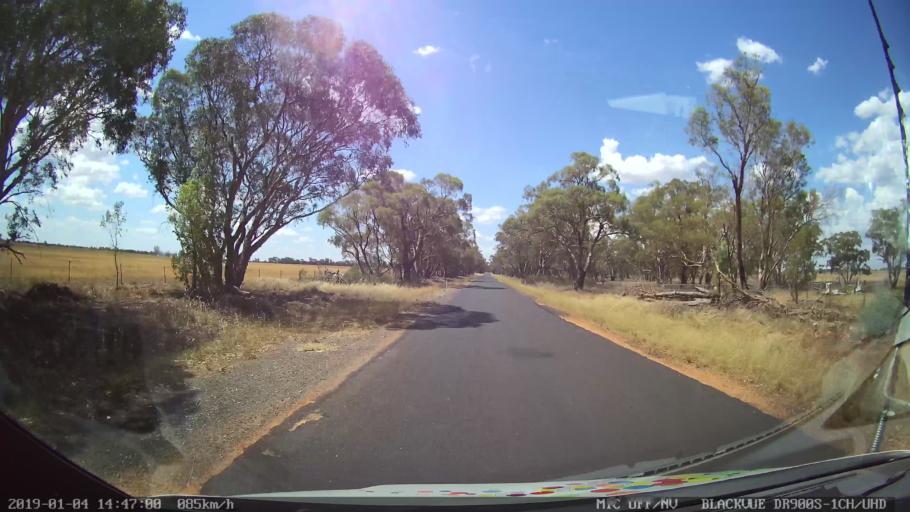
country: AU
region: New South Wales
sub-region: Dubbo Municipality
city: Dubbo
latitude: -32.0745
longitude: 148.6593
